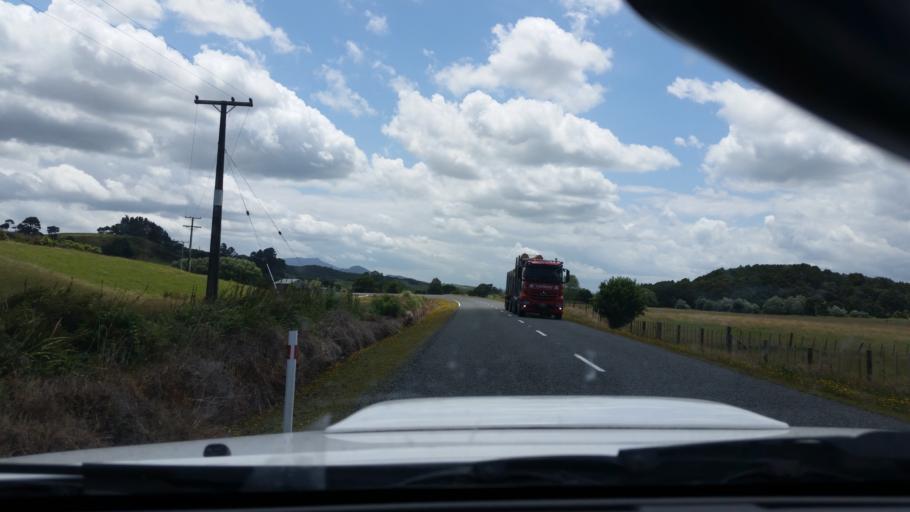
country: NZ
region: Northland
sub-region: Kaipara District
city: Dargaville
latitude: -35.9030
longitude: 173.8438
